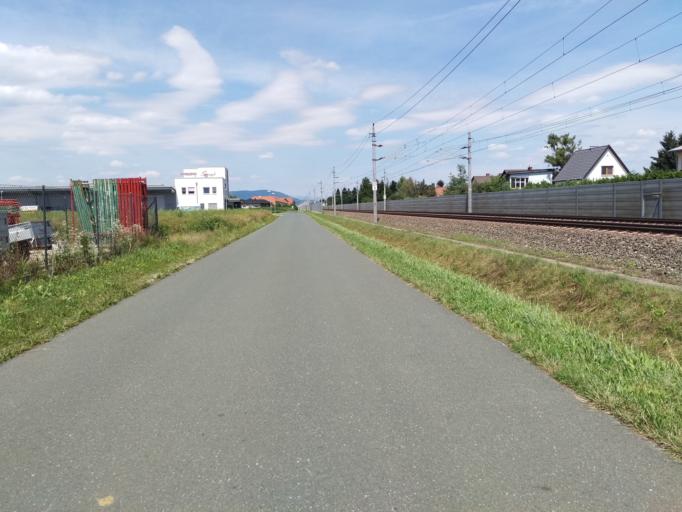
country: AT
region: Styria
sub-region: Politischer Bezirk Graz-Umgebung
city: Gossendorf
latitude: 46.9856
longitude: 15.4569
